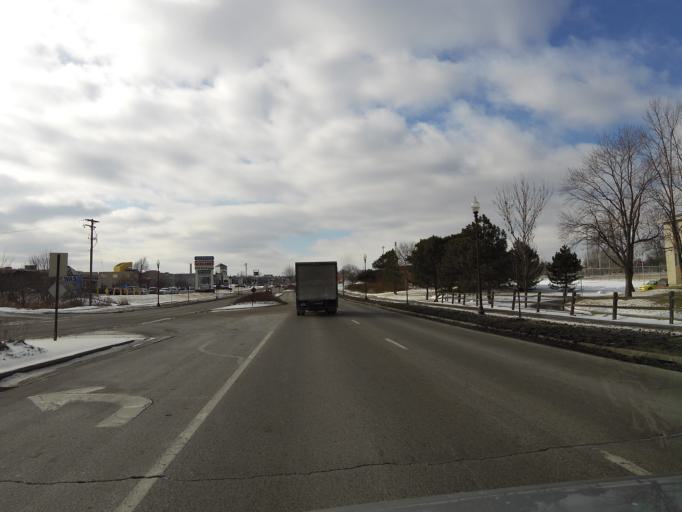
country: US
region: Minnesota
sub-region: Hennepin County
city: Minnetonka Mills
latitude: 44.9209
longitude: -93.4160
